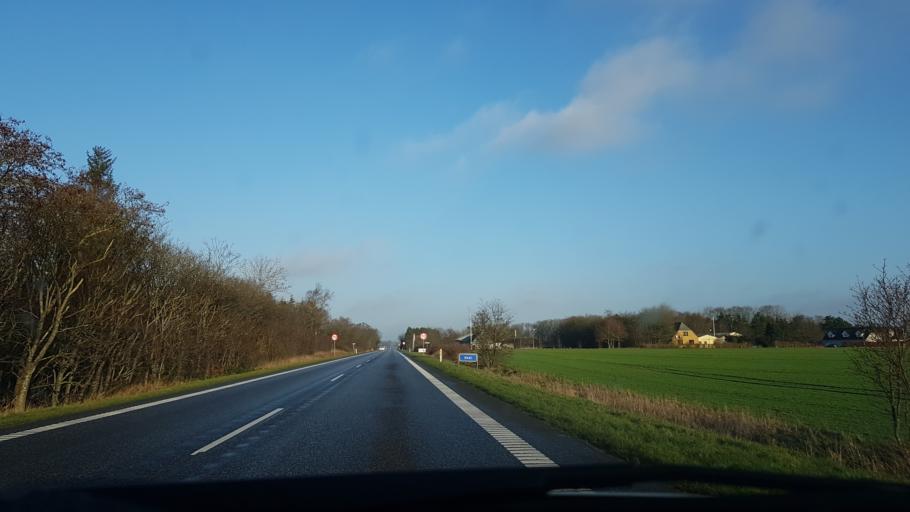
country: DK
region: South Denmark
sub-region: Tonder Kommune
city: Toftlund
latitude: 55.2304
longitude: 9.1187
